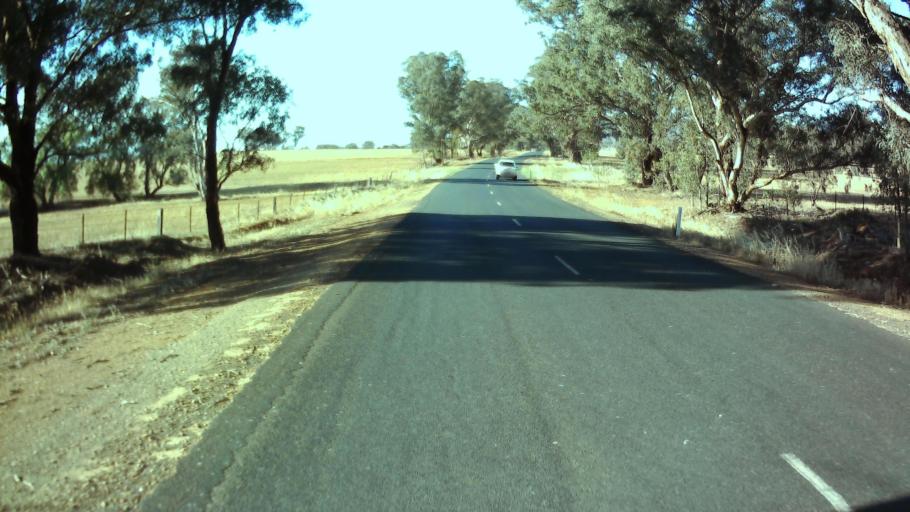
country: AU
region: New South Wales
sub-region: Weddin
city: Grenfell
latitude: -33.9173
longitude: 148.1420
